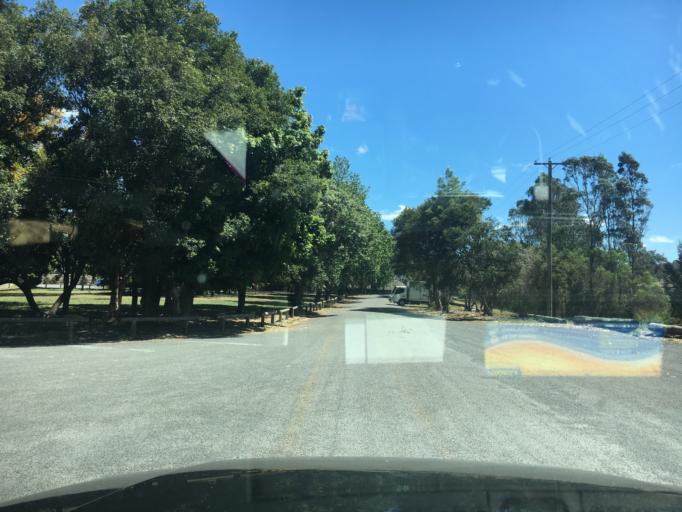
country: AU
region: New South Wales
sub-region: Singleton
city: Singleton
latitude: -32.5641
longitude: 151.1613
